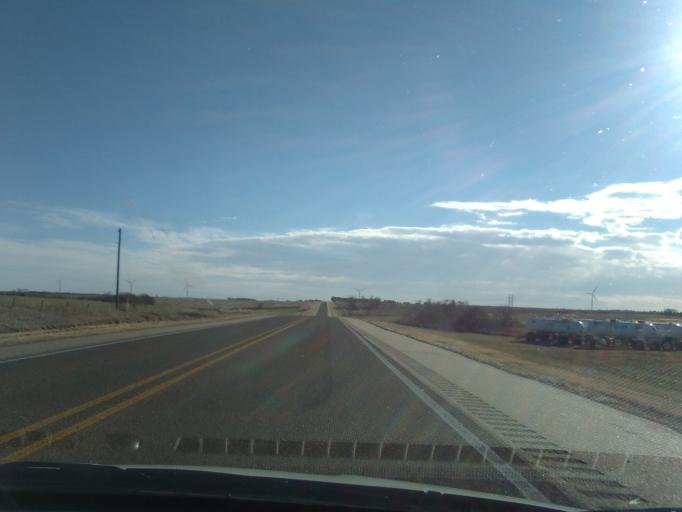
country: US
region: Nebraska
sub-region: Webster County
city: Red Cloud
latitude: 40.3194
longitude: -98.4441
